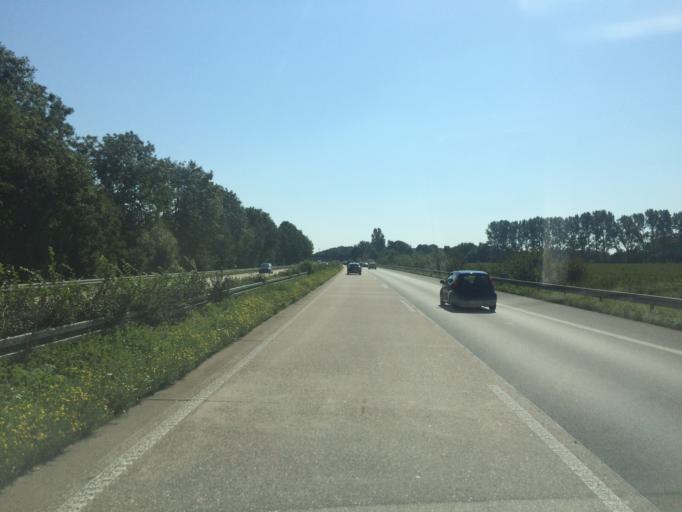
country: DE
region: North Rhine-Westphalia
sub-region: Regierungsbezirk Munster
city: Ascheberg
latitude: 51.8375
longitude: 7.5898
